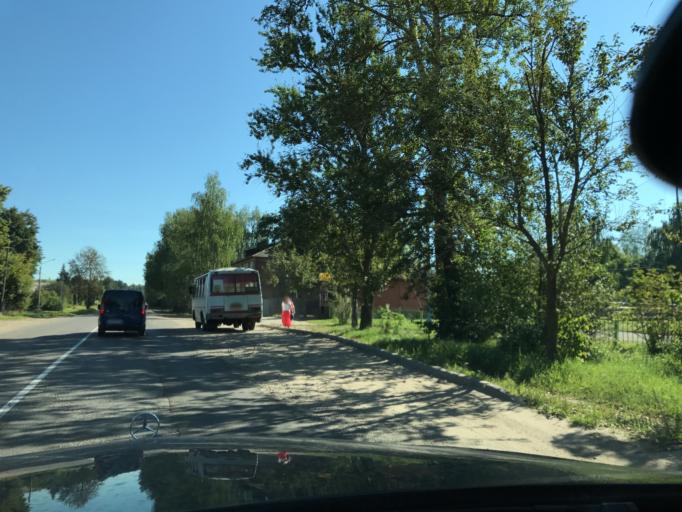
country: RU
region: Vladimir
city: Kirzhach
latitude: 56.1667
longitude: 38.8874
